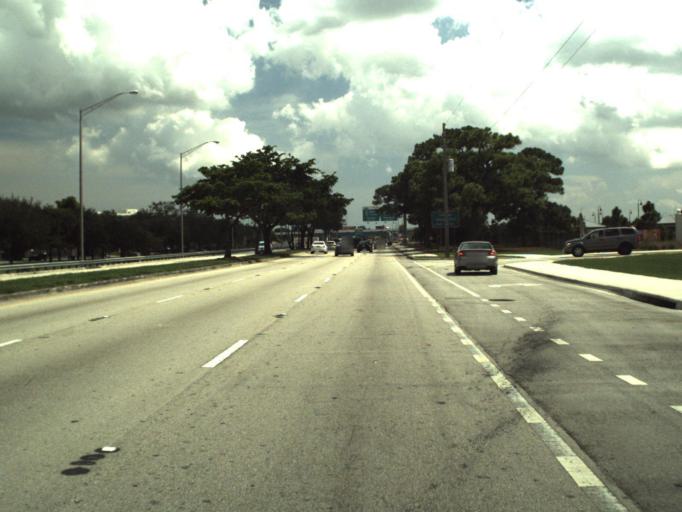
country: US
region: Florida
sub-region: Miami-Dade County
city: Lake Lucerne
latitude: 25.9780
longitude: -80.2472
